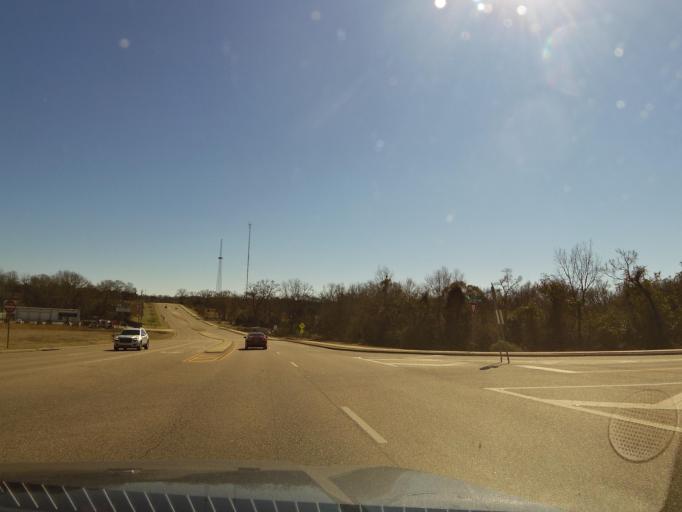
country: US
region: Alabama
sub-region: Autauga County
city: Prattville
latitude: 32.4824
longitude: -86.4128
